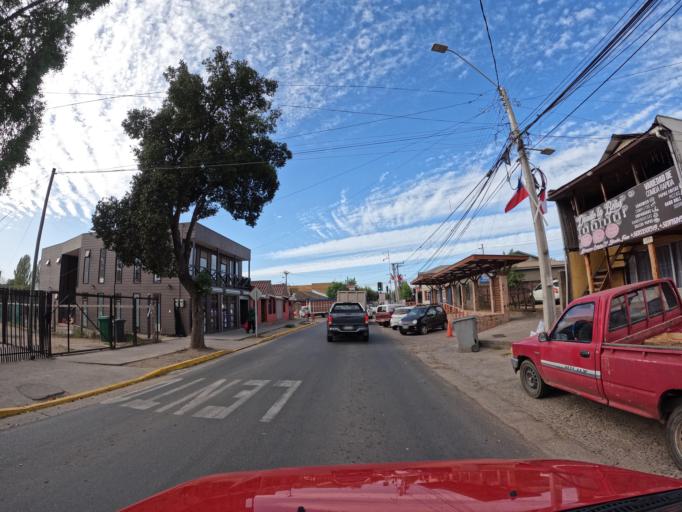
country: CL
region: Valparaiso
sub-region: San Antonio Province
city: San Antonio
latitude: -34.1162
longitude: -71.7268
